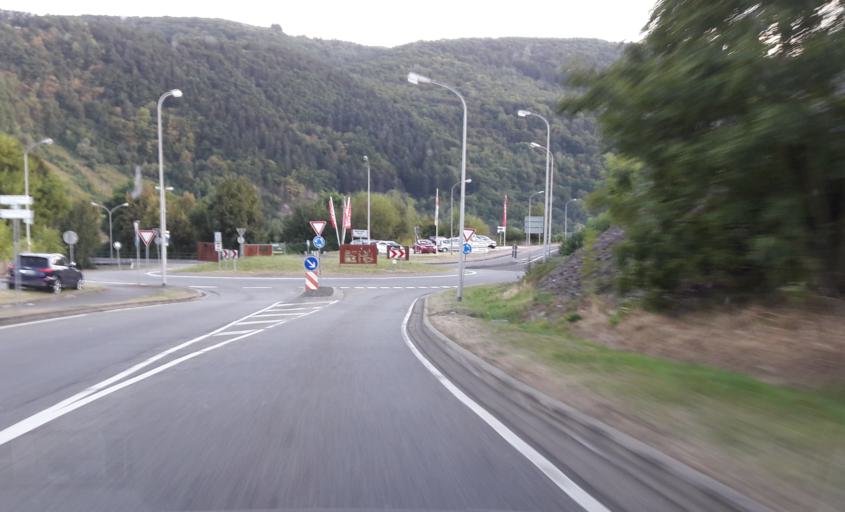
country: DE
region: Rheinland-Pfalz
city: Zell
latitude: 50.0195
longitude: 7.1762
